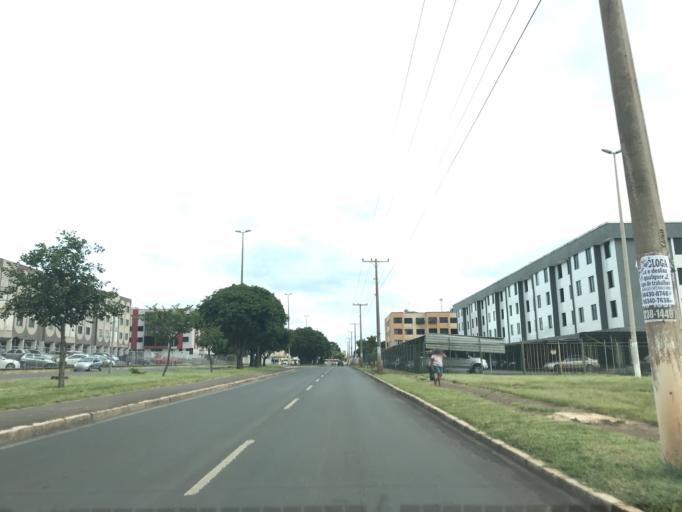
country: BR
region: Federal District
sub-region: Brasilia
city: Brasilia
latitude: -15.8131
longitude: -48.0890
